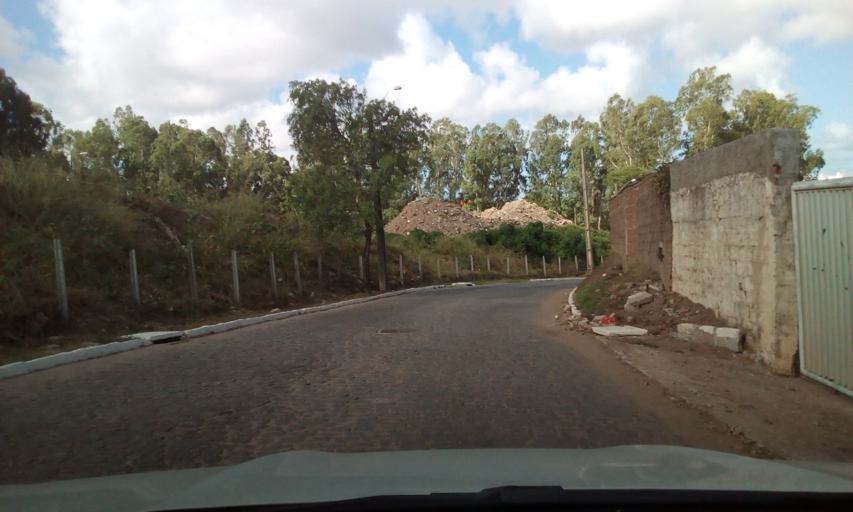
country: BR
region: Paraiba
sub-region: Joao Pessoa
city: Joao Pessoa
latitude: -7.1756
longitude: -34.8492
